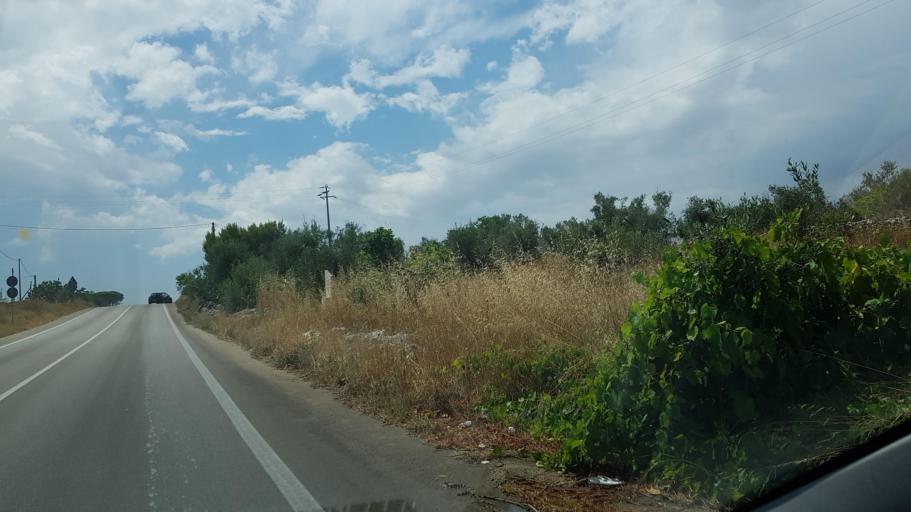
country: IT
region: Apulia
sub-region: Provincia di Lecce
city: Ruffano
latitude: 39.9611
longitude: 18.2547
